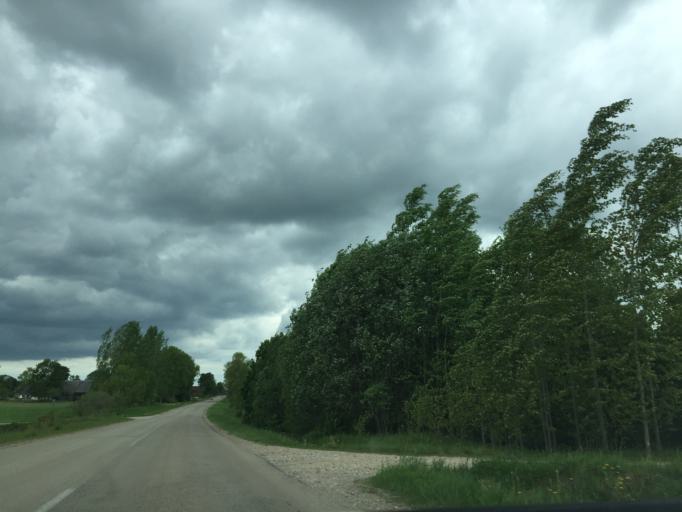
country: LV
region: Dagda
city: Dagda
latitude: 56.1034
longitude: 27.5013
